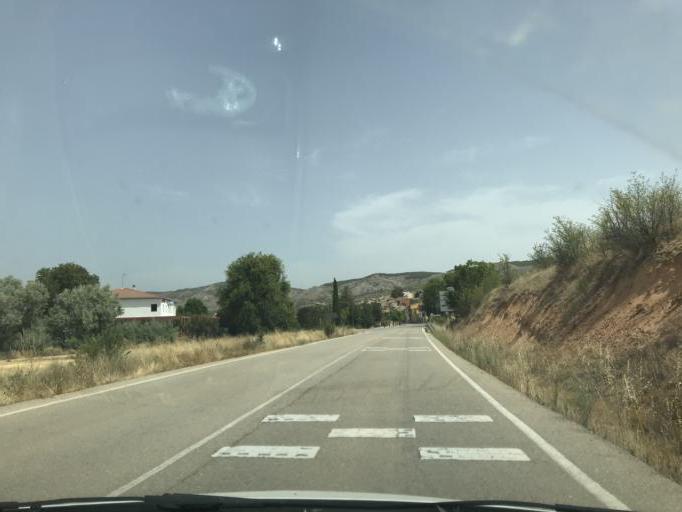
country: ES
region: Castille-La Mancha
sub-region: Provincia de Cuenca
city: Albalate de las Nogueras
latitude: 40.3616
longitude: -2.2802
